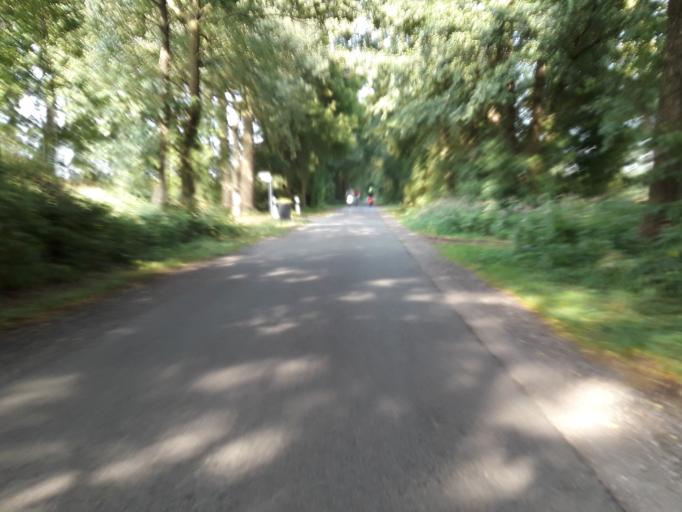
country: DE
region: North Rhine-Westphalia
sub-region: Regierungsbezirk Detmold
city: Hovelhof
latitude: 51.7877
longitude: 8.6607
